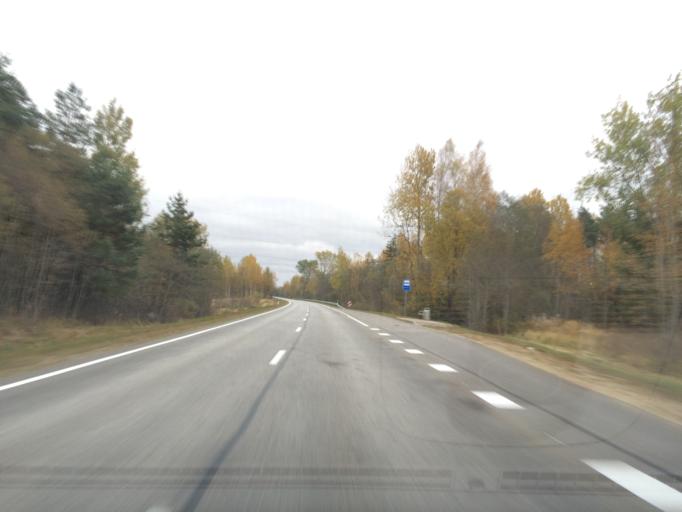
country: LV
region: Livani
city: Livani
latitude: 56.5293
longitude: 26.3697
